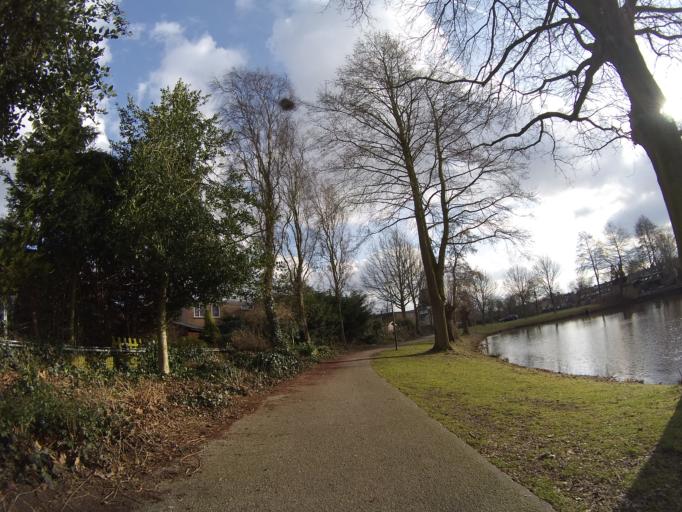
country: NL
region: Utrecht
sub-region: Gemeente Soest
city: Soest
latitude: 52.1661
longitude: 5.2801
